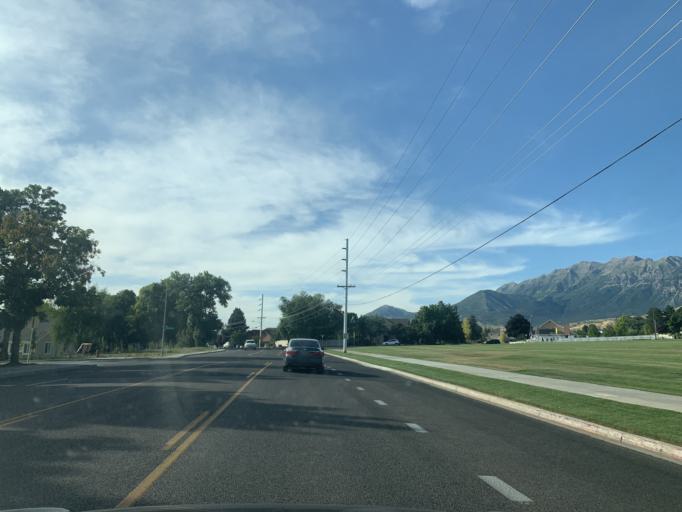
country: US
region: Utah
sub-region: Utah County
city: Provo
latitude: 40.2617
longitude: -111.6448
